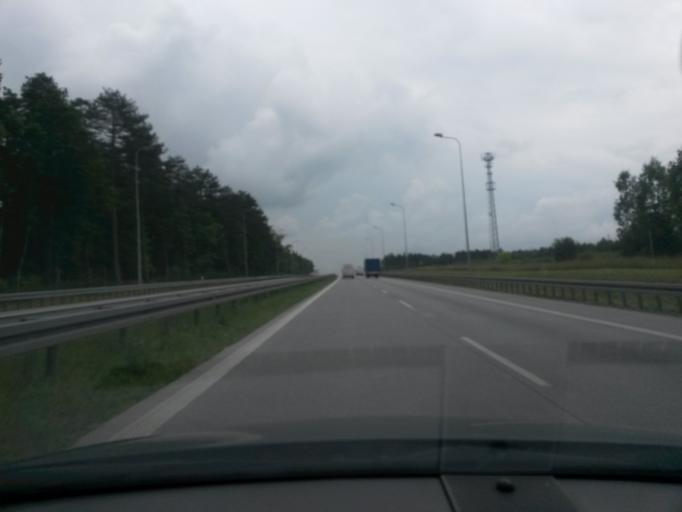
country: PL
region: Lodz Voivodeship
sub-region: Powiat rawski
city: Rawa Mazowiecka
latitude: 51.8228
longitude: 20.3209
